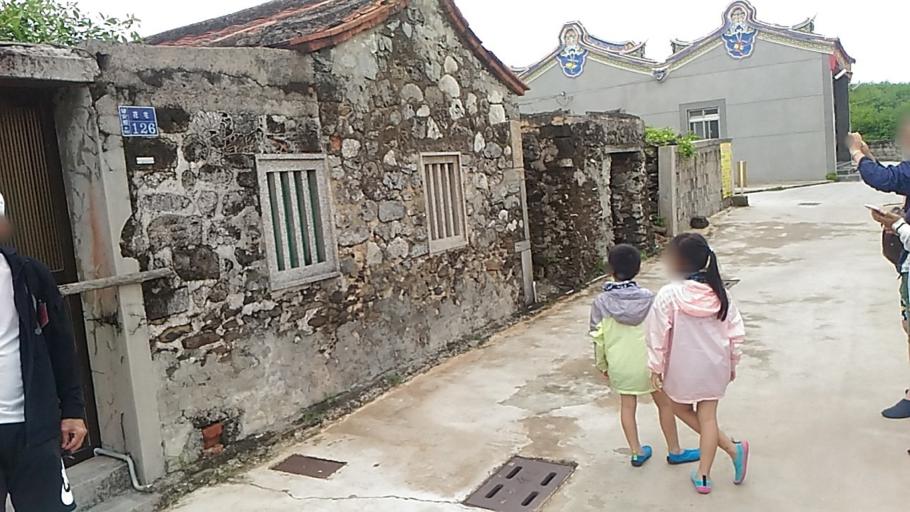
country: TW
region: Taiwan
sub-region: Penghu
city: Ma-kung
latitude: 23.3704
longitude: 119.4952
